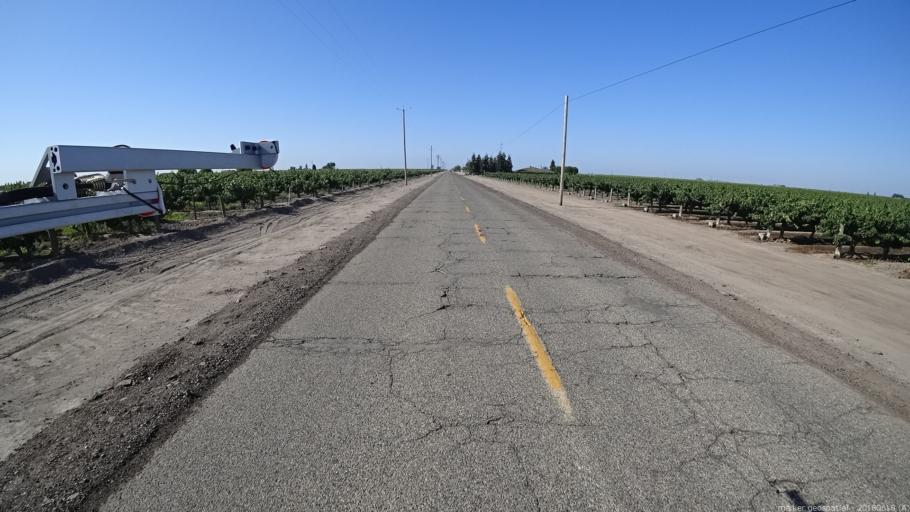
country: US
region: California
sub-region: Madera County
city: Parkwood
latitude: 36.8634
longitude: -120.1284
